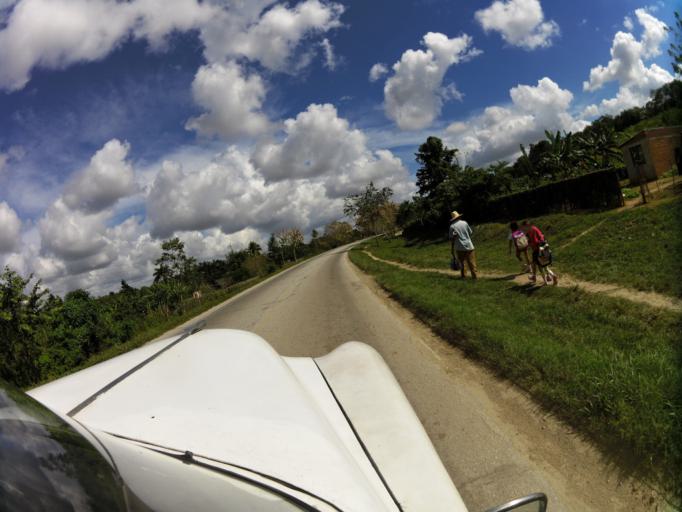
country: CU
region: Holguin
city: Cacocum
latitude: 20.8670
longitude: -76.4350
